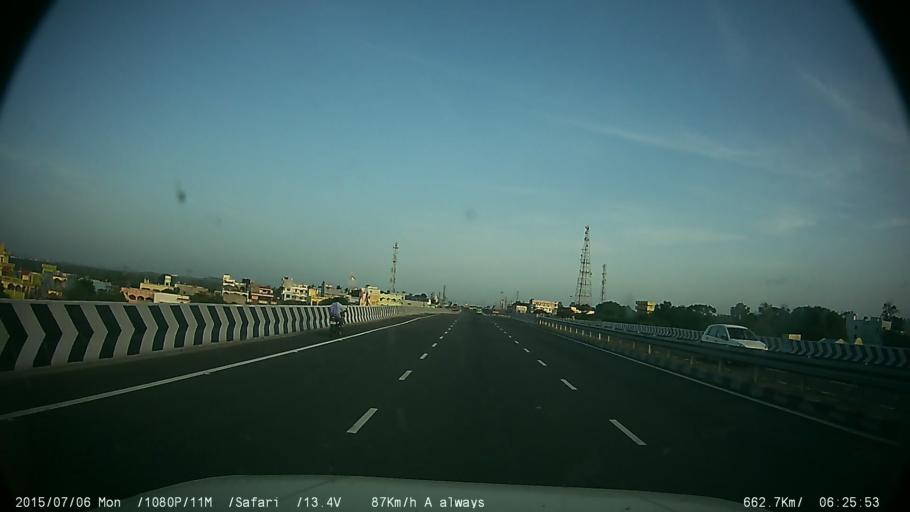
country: IN
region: Tamil Nadu
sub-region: Krishnagiri
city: Kelamangalam
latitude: 12.6628
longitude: 78.0091
